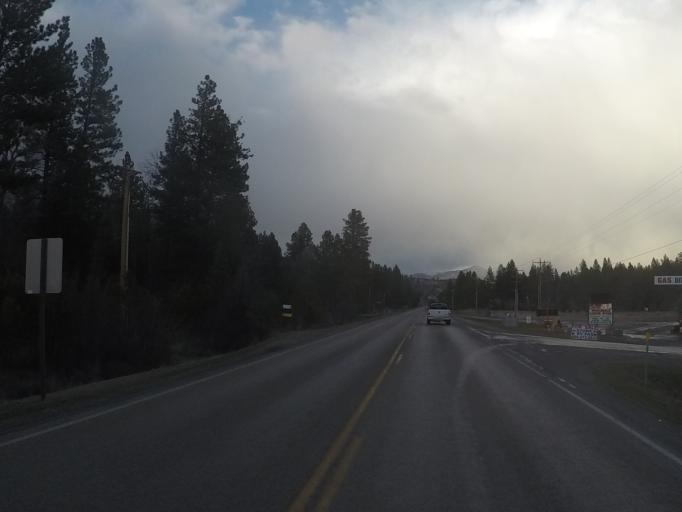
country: US
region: Montana
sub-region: Missoula County
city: Lolo
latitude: 46.7458
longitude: -114.1440
